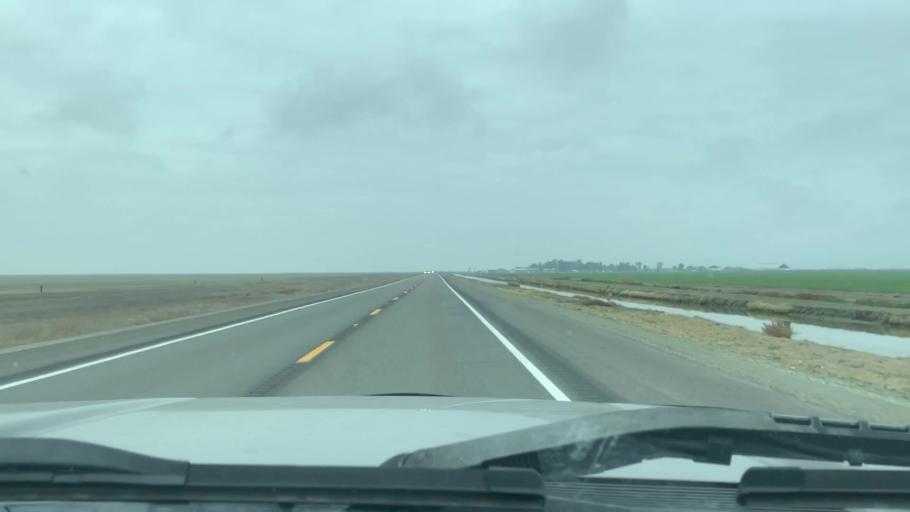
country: US
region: California
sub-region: Kings County
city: Stratford
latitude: 36.1091
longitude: -119.9012
